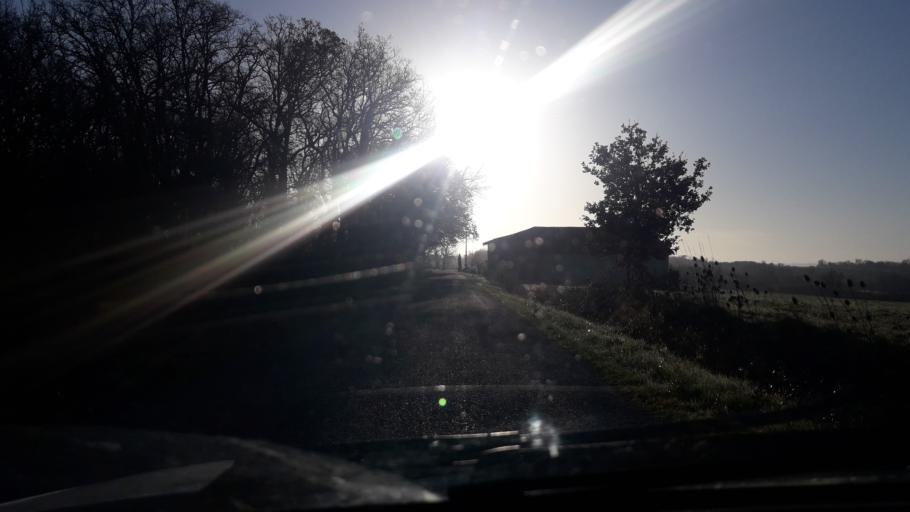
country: FR
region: Midi-Pyrenees
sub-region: Departement du Gers
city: Gimont
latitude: 43.6517
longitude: 0.9844
